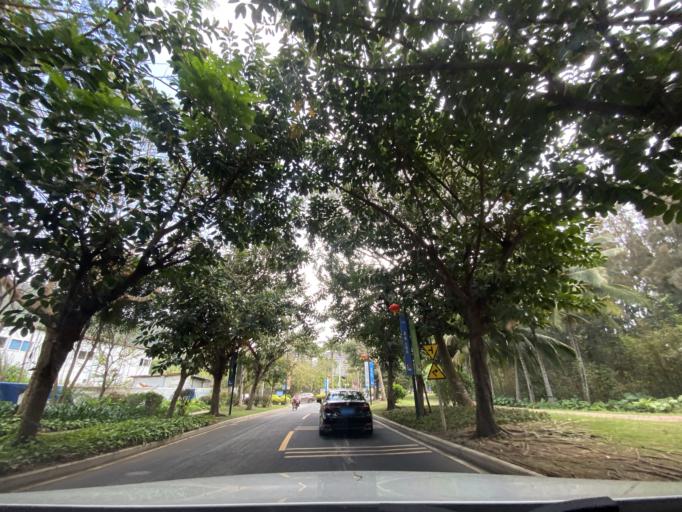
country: CN
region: Hainan
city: Liji
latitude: 18.6694
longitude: 110.2671
